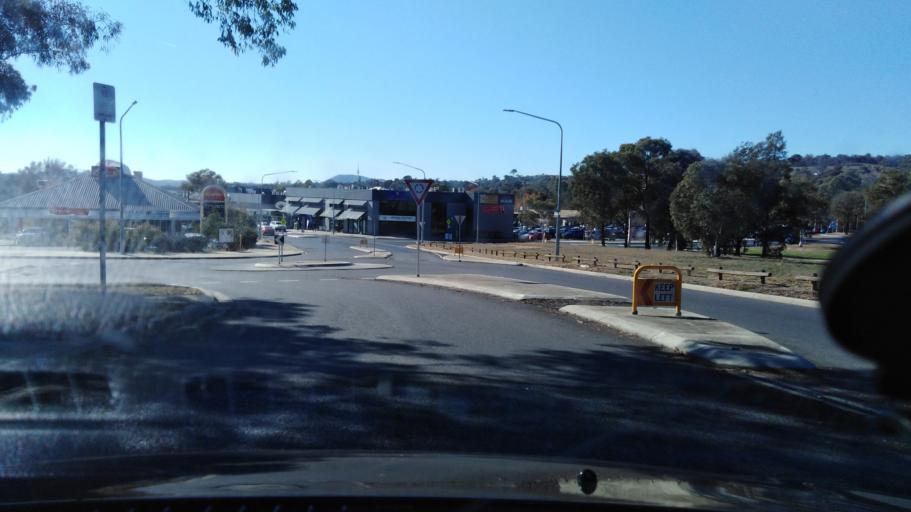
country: AU
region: Australian Capital Territory
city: Forrest
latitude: -35.3431
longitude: 149.0518
